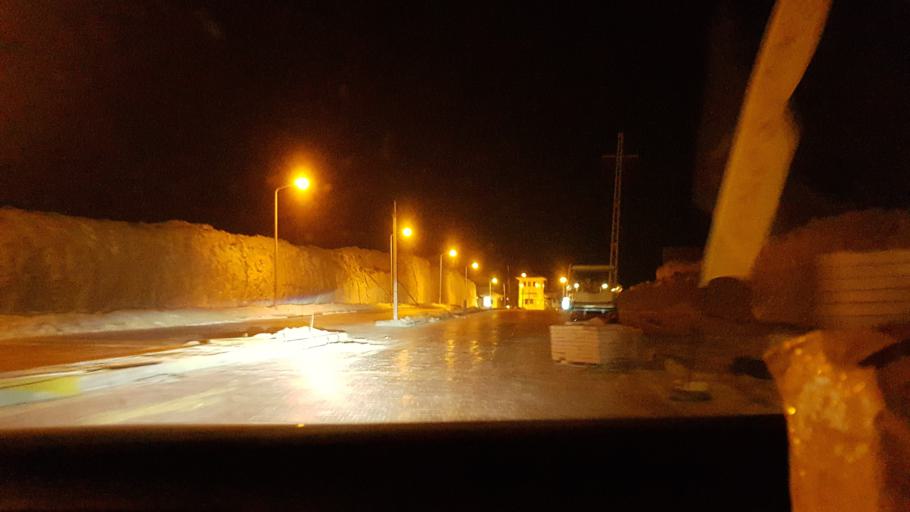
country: EG
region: Muhafazat Matruh
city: Al `Alamayn
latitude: 31.0638
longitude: 28.3610
